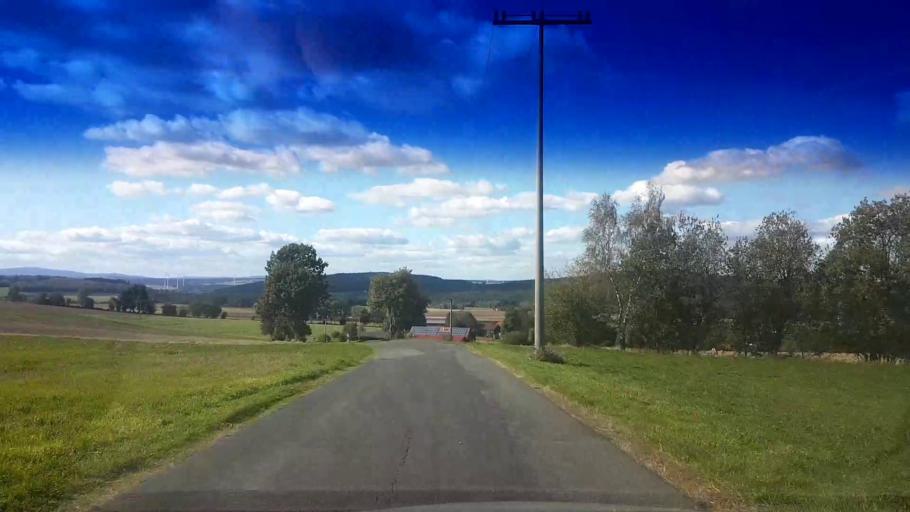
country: DE
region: Bavaria
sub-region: Upper Franconia
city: Schirnding
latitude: 50.0216
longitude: 12.2411
